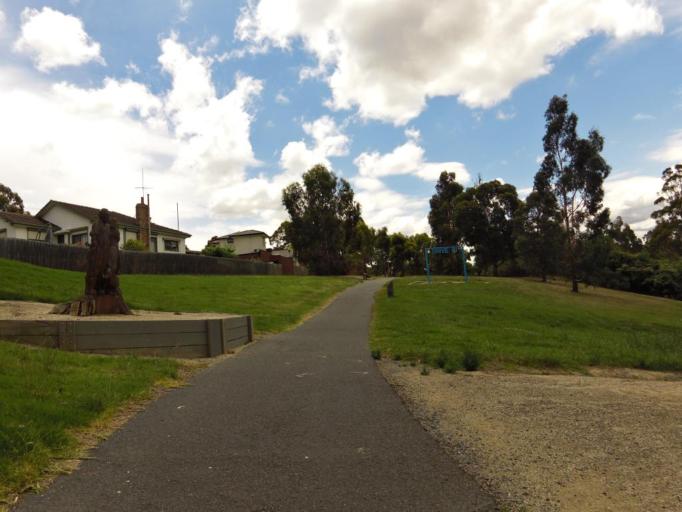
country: AU
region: Victoria
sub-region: Whitehorse
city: Burwood
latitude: -37.8516
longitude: 145.1094
